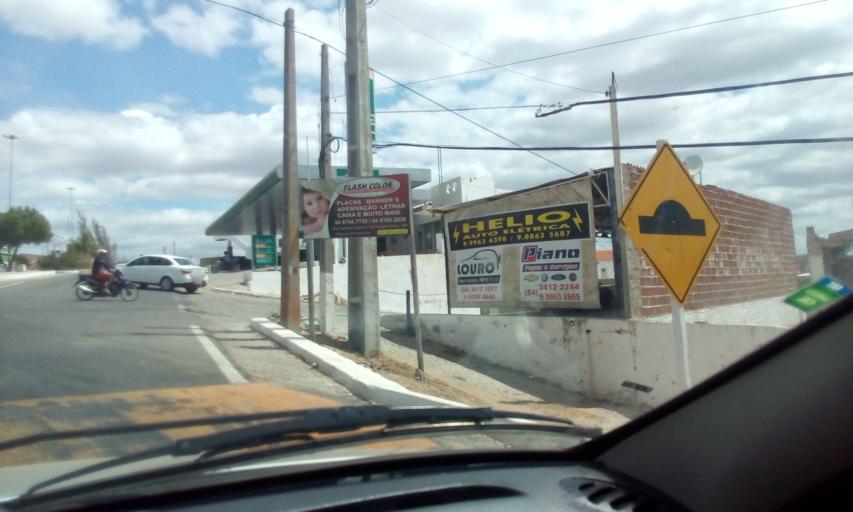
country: BR
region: Rio Grande do Norte
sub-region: Currais Novos
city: Currais Novos
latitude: -6.2687
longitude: -36.5227
